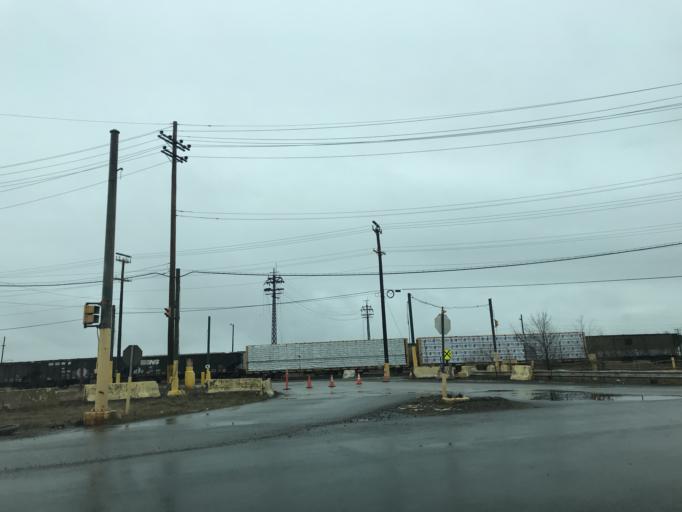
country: US
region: Maryland
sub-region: Baltimore County
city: Dundalk
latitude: 39.2265
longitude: -76.4909
